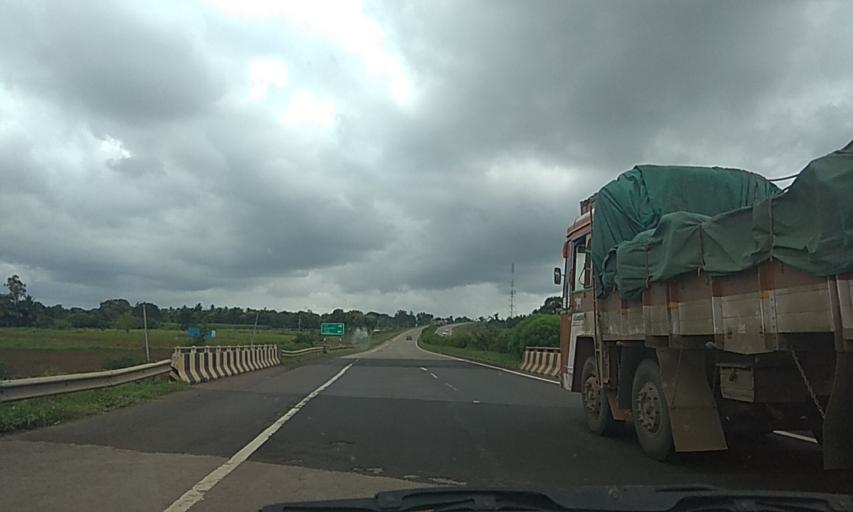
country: IN
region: Karnataka
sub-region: Belgaum
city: Sankeshwar
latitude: 16.2507
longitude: 74.4759
